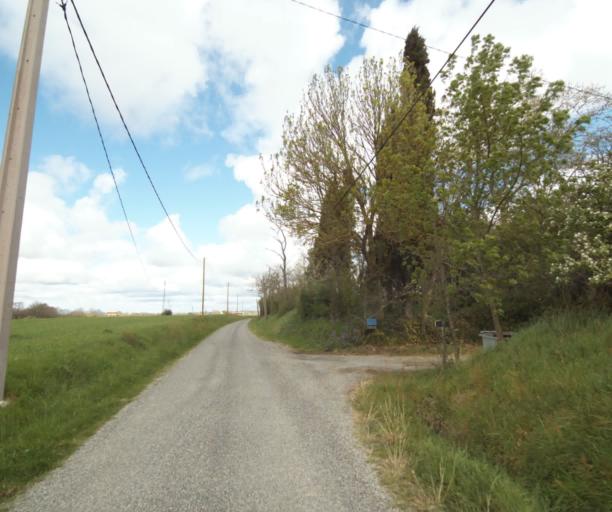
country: FR
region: Midi-Pyrenees
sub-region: Departement de l'Ariege
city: Saverdun
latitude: 43.2152
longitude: 1.5815
